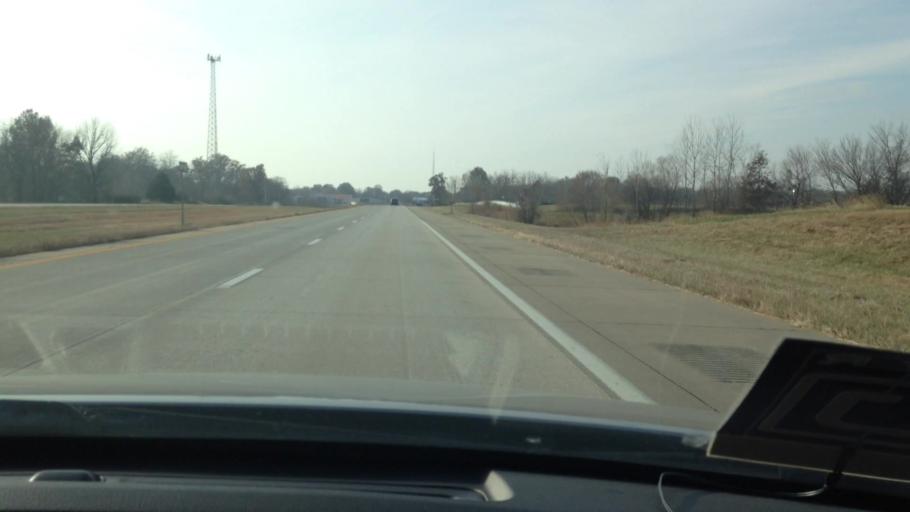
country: US
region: Missouri
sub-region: Cass County
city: Garden City
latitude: 38.4641
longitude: -93.9876
